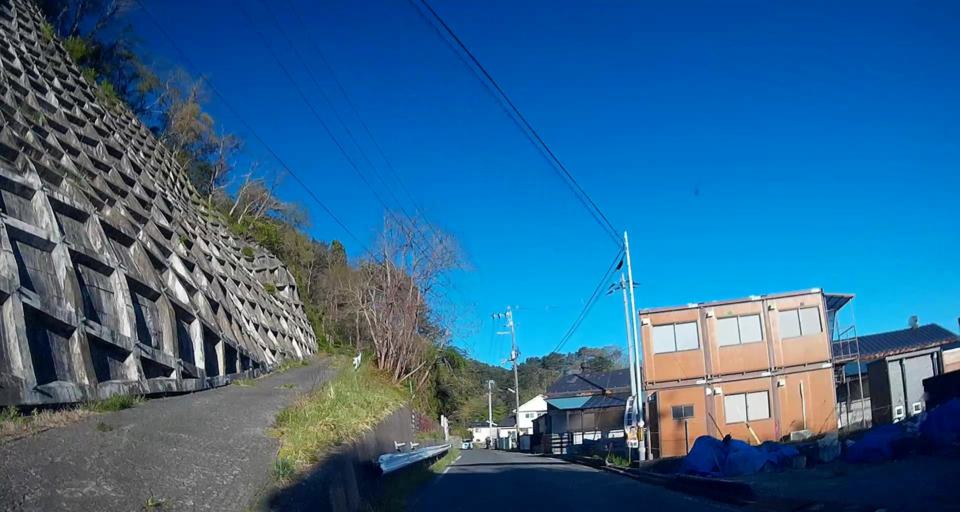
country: JP
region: Iwate
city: Miyako
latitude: 39.6458
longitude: 141.9728
